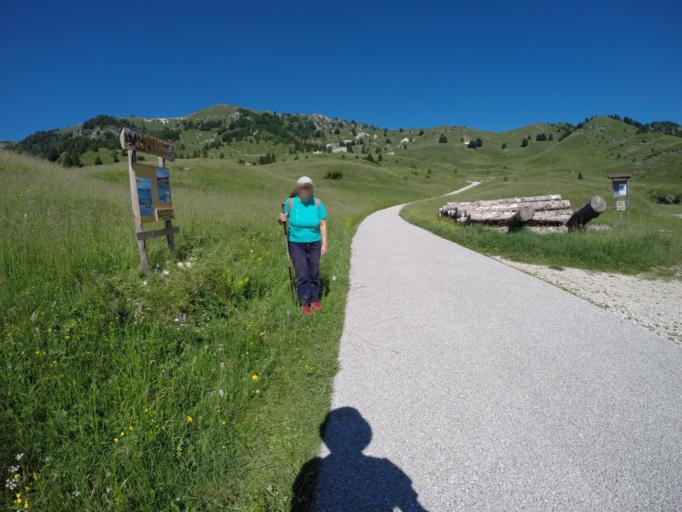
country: IT
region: Veneto
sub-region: Provincia di Treviso
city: Crespano del Grappa
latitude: 45.8828
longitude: 11.8113
